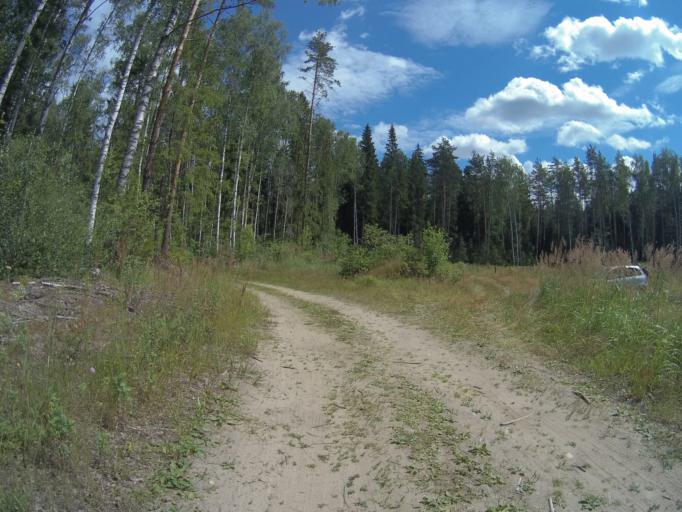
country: RU
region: Vladimir
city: Orgtrud
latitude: 56.0177
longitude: 40.5922
